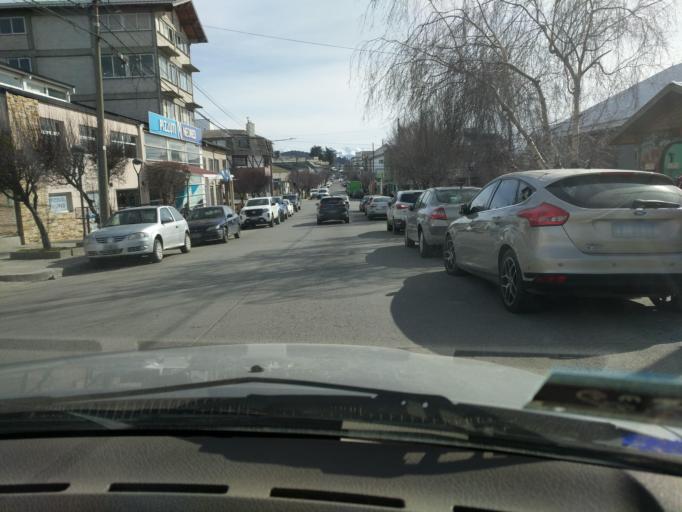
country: AR
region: Rio Negro
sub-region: Departamento de Bariloche
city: San Carlos de Bariloche
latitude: -41.1374
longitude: -71.2937
